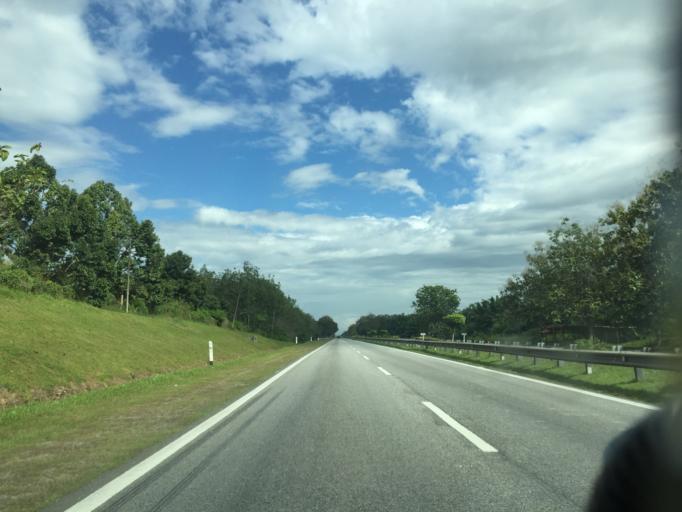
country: MY
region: Kedah
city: Jitra
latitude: 6.3790
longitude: 100.4243
